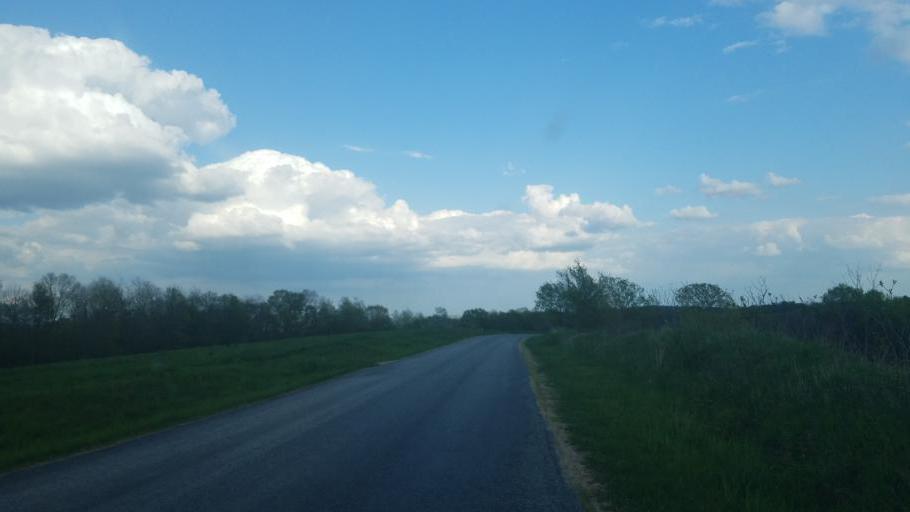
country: US
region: Wisconsin
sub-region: Vernon County
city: Hillsboro
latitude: 43.6838
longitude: -90.3767
